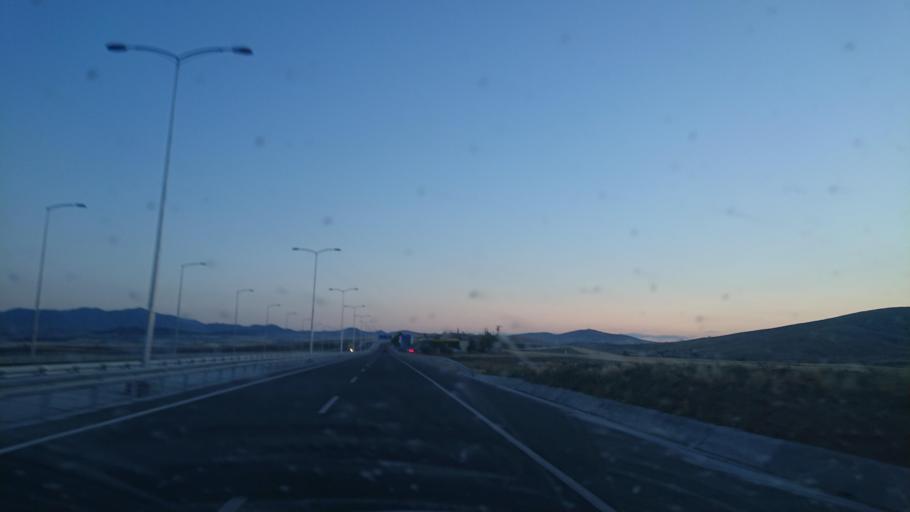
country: TR
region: Aksaray
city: Balci
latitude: 38.7773
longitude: 34.1118
